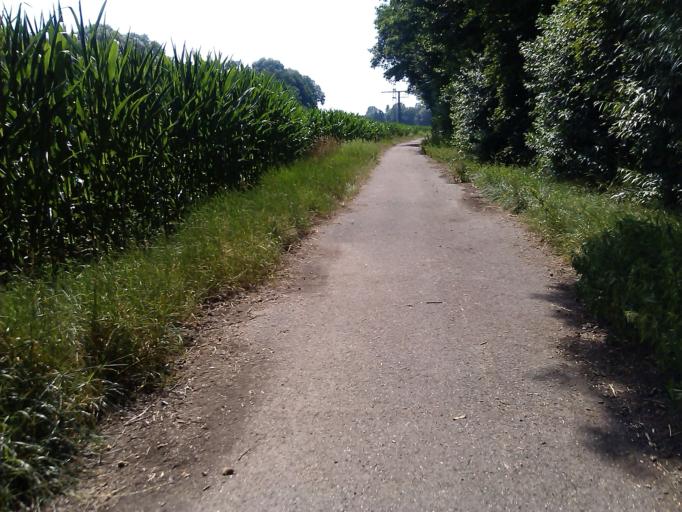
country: DE
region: Baden-Wuerttemberg
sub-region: Regierungsbezirk Stuttgart
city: Guglingen
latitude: 49.0651
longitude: 8.9932
